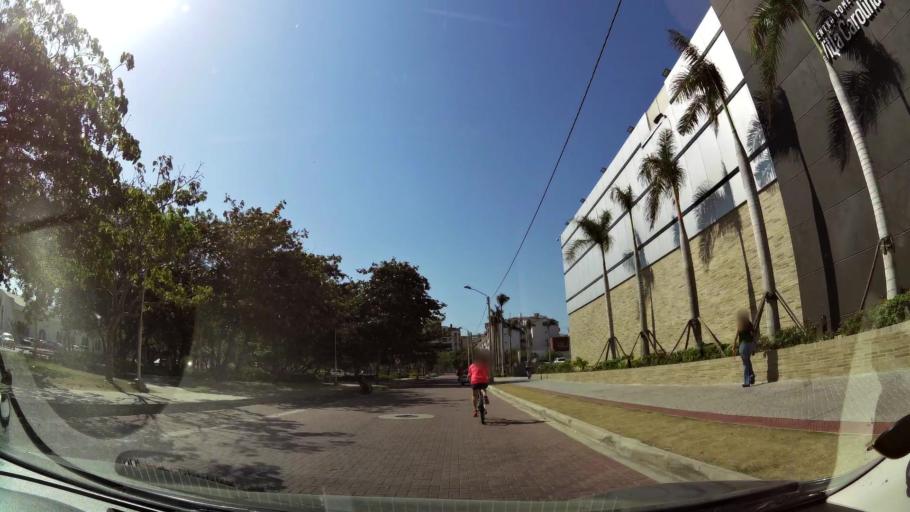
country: CO
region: Atlantico
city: Barranquilla
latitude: 11.0213
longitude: -74.8164
